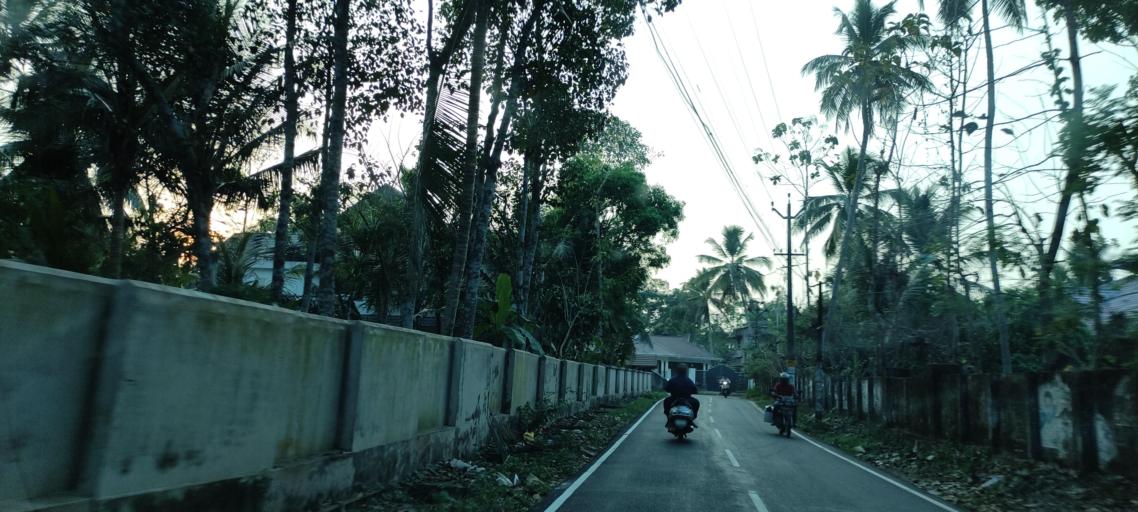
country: IN
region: Kerala
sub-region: Alappuzha
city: Mavelikara
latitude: 9.2683
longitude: 76.5414
